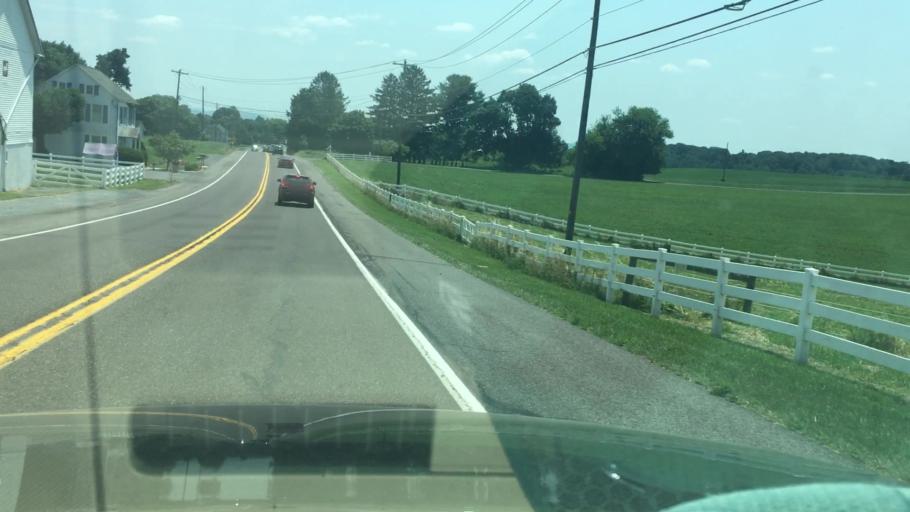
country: US
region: Pennsylvania
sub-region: Lehigh County
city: Schnecksville
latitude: 40.6103
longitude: -75.6484
